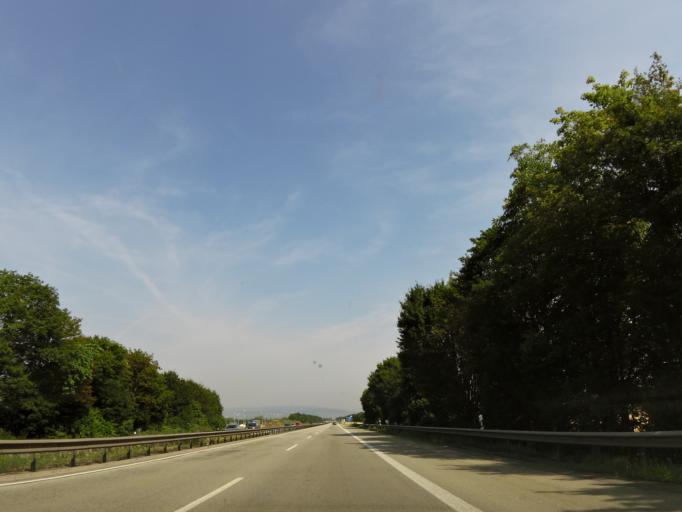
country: DE
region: Rheinland-Pfalz
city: Zotzenheim
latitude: 49.8629
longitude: 7.9677
